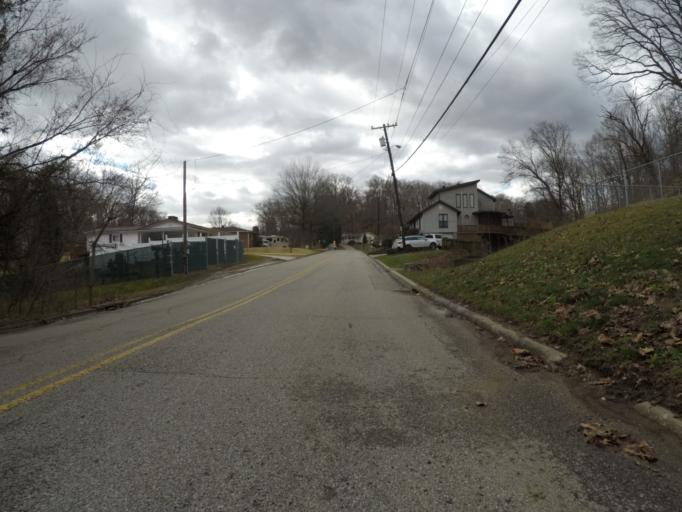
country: US
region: West Virginia
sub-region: Cabell County
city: Pea Ridge
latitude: 38.4086
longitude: -82.3828
